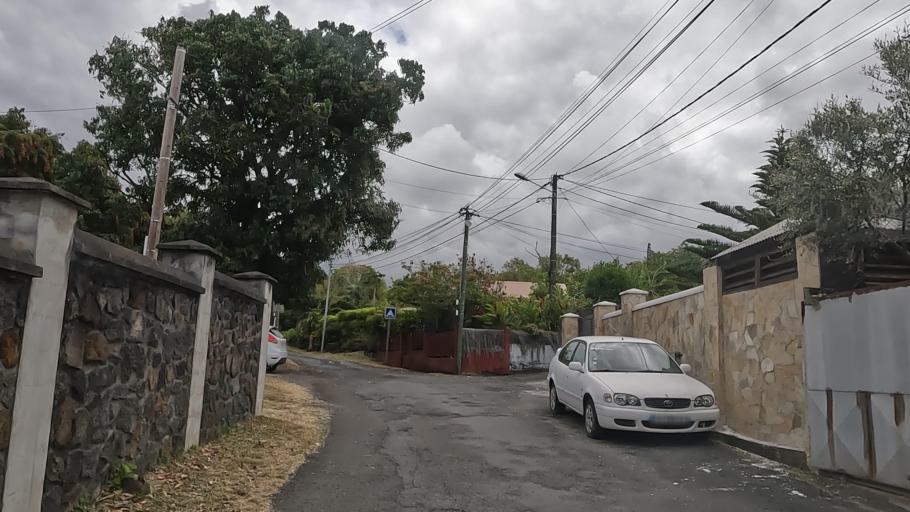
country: RE
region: Reunion
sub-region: Reunion
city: Saint-Benoit
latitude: -21.0912
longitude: 55.7452
